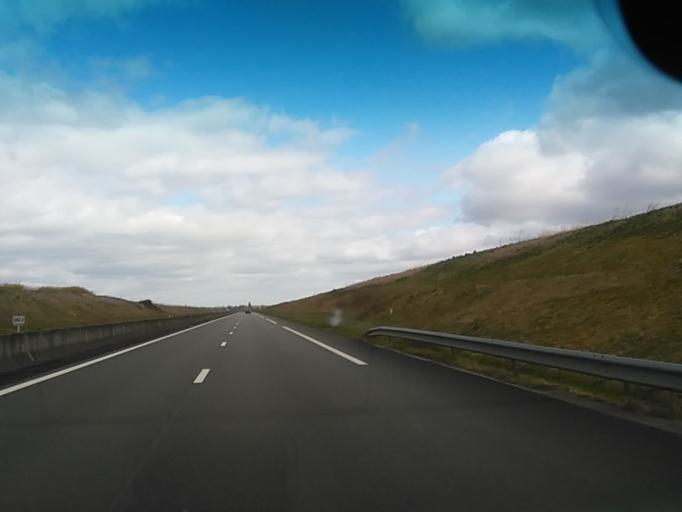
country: FR
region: Haute-Normandie
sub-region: Departement de l'Eure
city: Thiberville
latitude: 49.1098
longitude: 0.5157
